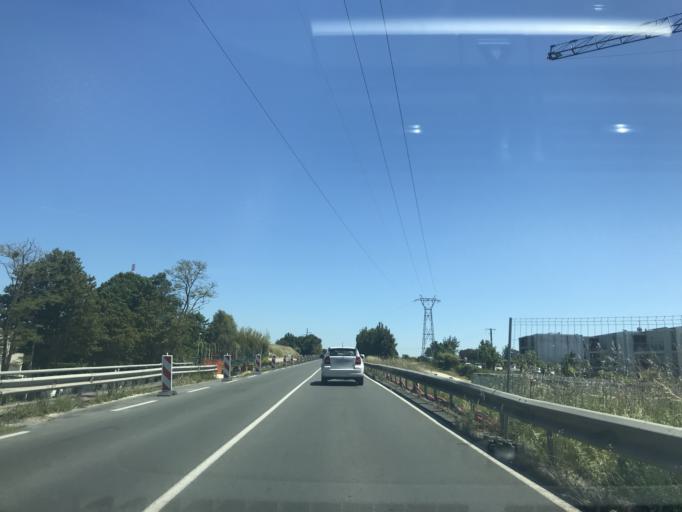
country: FR
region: Poitou-Charentes
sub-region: Departement de la Charente-Maritime
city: Royan
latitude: 45.6420
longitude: -1.0363
